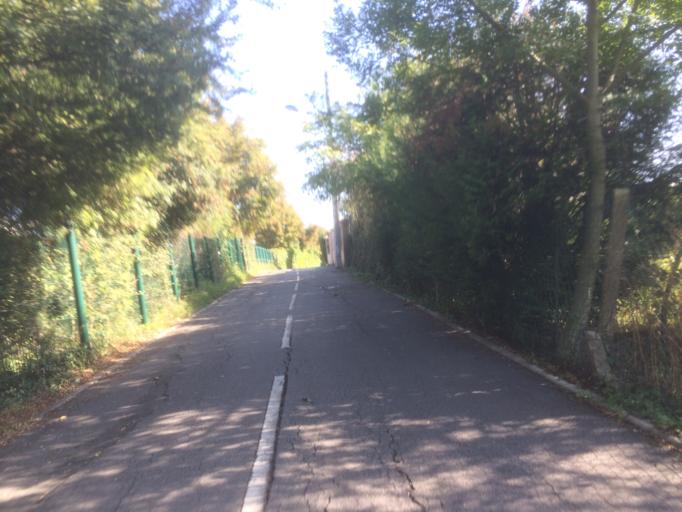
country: FR
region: Ile-de-France
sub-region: Departement de l'Essonne
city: Longjumeau
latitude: 48.6971
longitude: 2.3141
